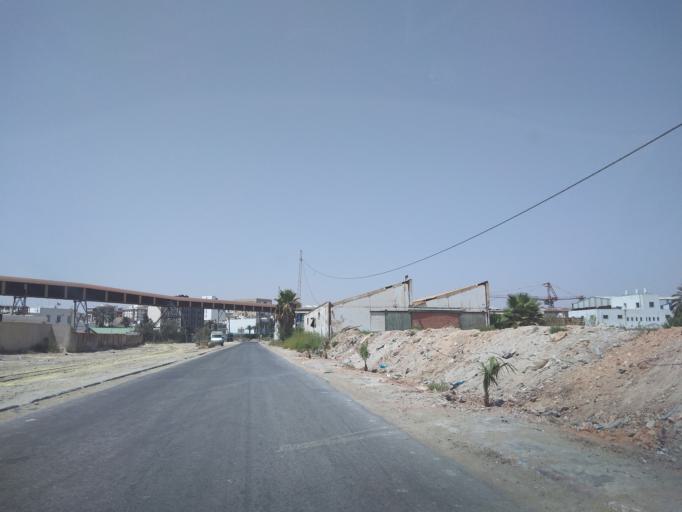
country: TN
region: Safaqis
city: Sfax
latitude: 34.7326
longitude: 10.7724
